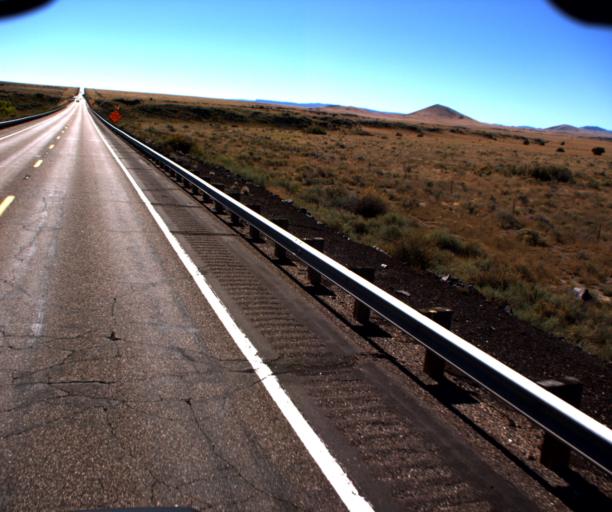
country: US
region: Arizona
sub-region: Apache County
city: Springerville
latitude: 34.2881
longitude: -109.3706
